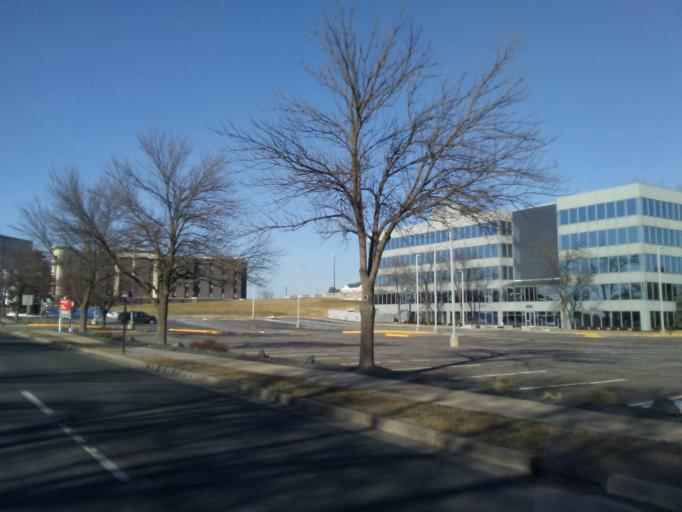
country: US
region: Minnesota
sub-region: Hennepin County
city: Edina
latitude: 44.8534
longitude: -93.3522
